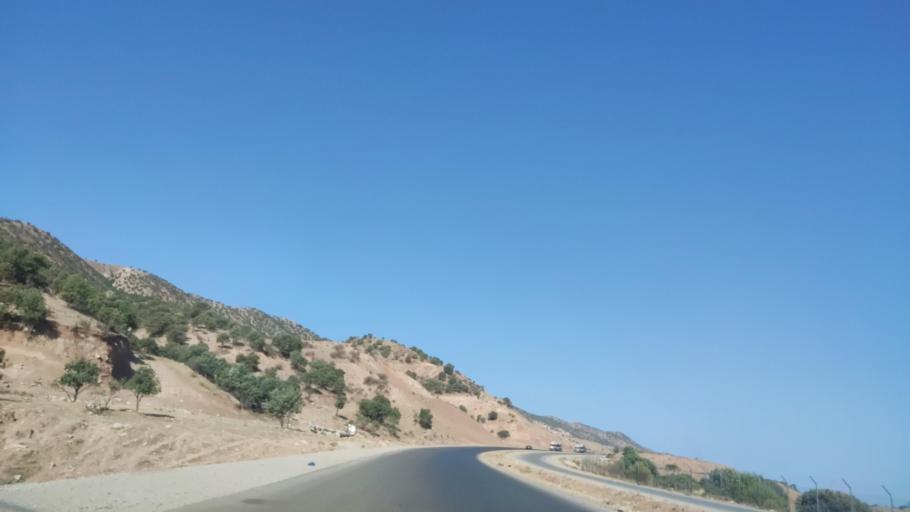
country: IQ
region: Arbil
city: Shaqlawah
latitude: 36.4312
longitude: 44.3158
